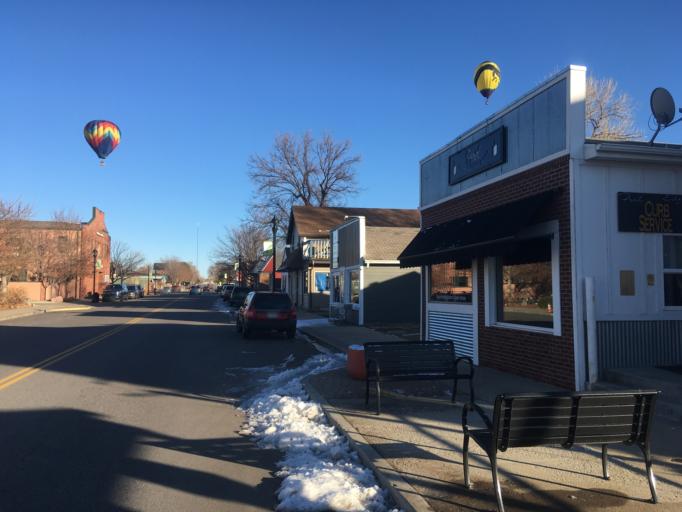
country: US
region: Colorado
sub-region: Weld County
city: Frederick
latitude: 40.0986
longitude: -104.9396
